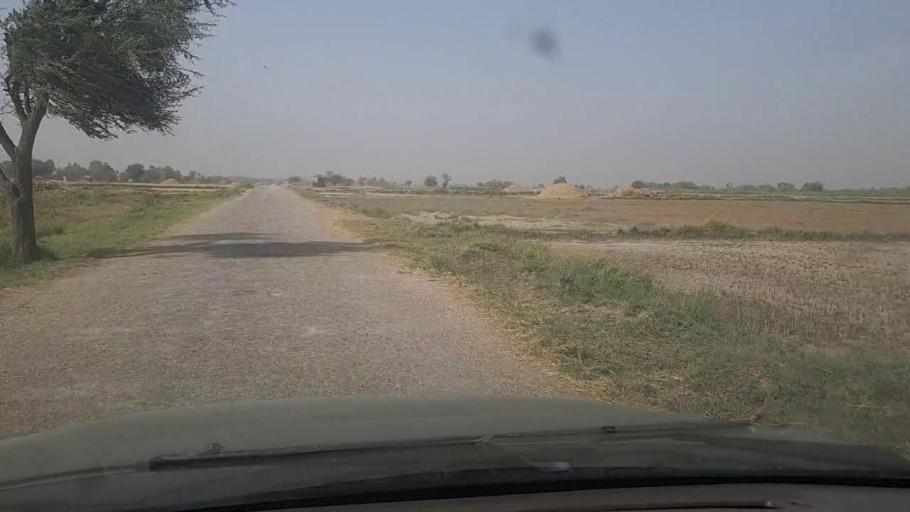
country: PK
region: Sindh
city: Garhi Yasin
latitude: 27.8837
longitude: 68.5721
